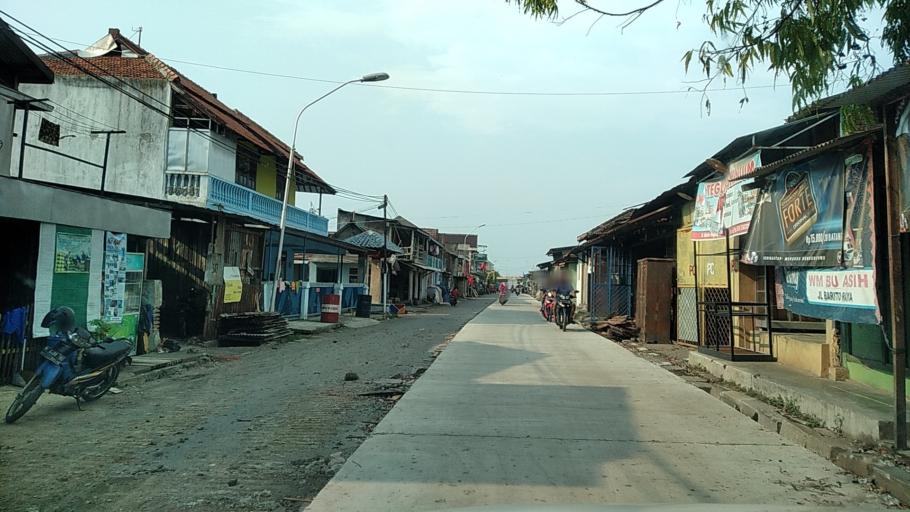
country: ID
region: Central Java
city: Semarang
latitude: -6.9755
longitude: 110.4417
